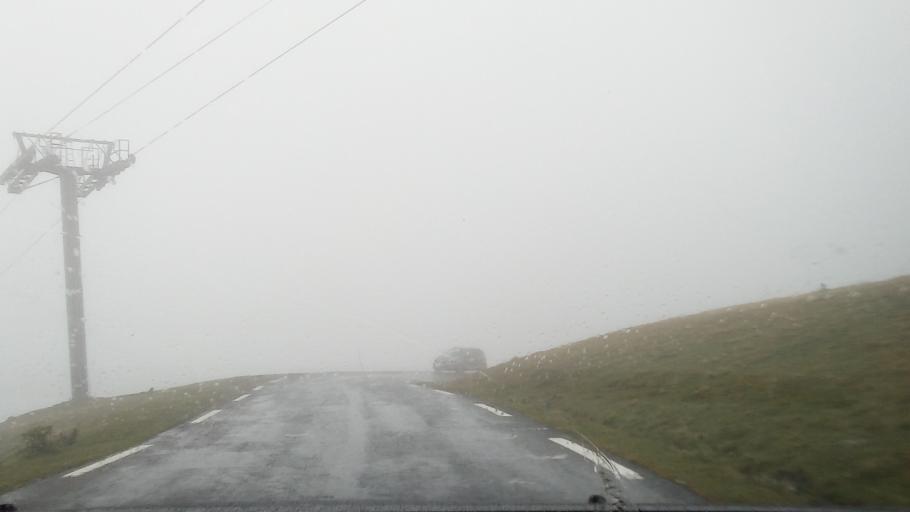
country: FR
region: Midi-Pyrenees
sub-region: Departement des Hautes-Pyrenees
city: Campan
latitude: 42.9093
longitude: 0.1561
